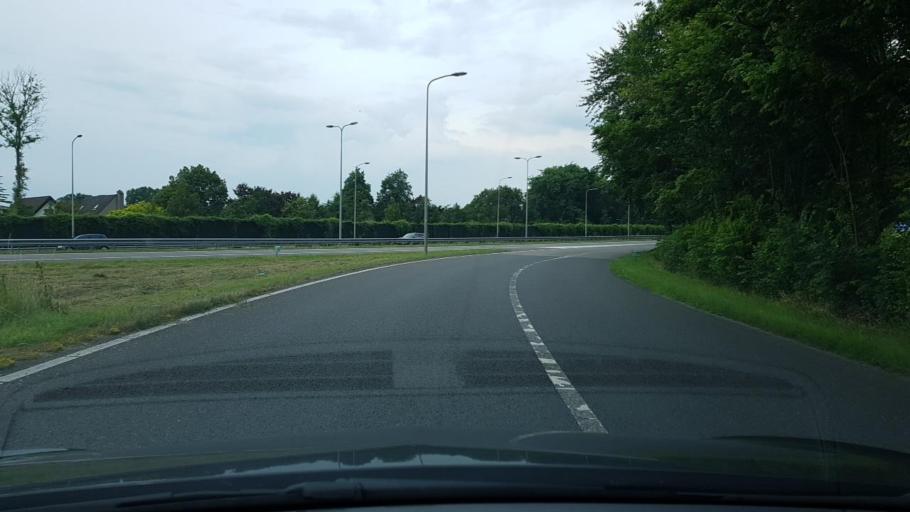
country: NL
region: South Holland
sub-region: Gemeente Katwijk
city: Katwijk aan den Rijn
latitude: 52.2046
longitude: 4.4304
